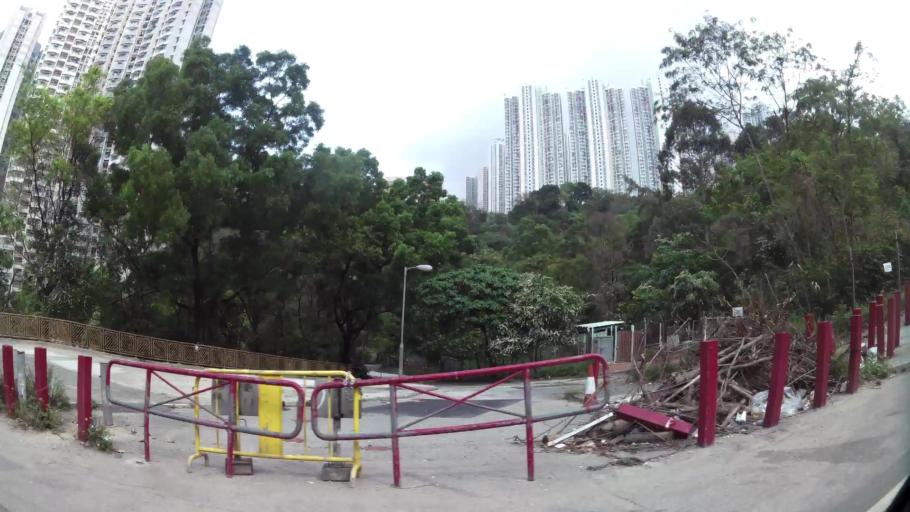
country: HK
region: Kowloon City
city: Kowloon
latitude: 22.3125
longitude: 114.2355
